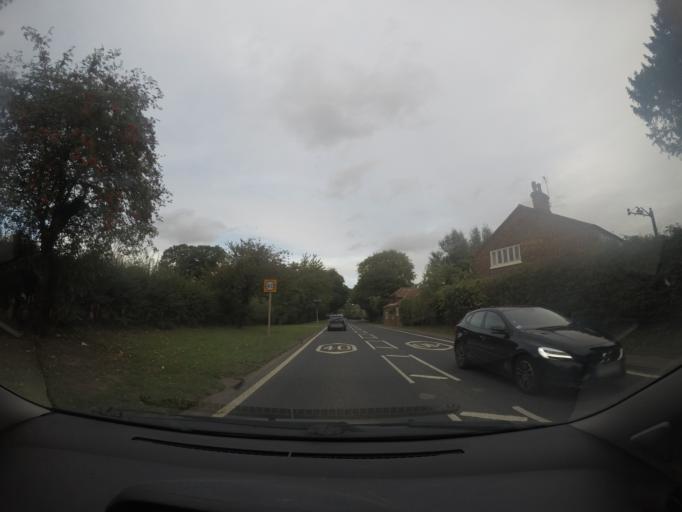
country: GB
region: England
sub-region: City of York
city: Deighton
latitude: 53.8775
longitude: -1.0449
